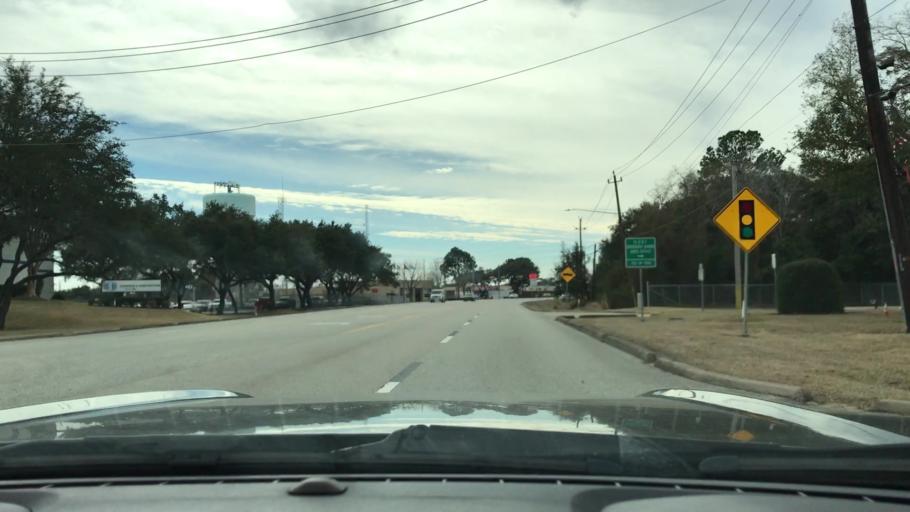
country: US
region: Texas
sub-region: Galveston County
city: Friendswood
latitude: 29.5922
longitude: -95.1803
